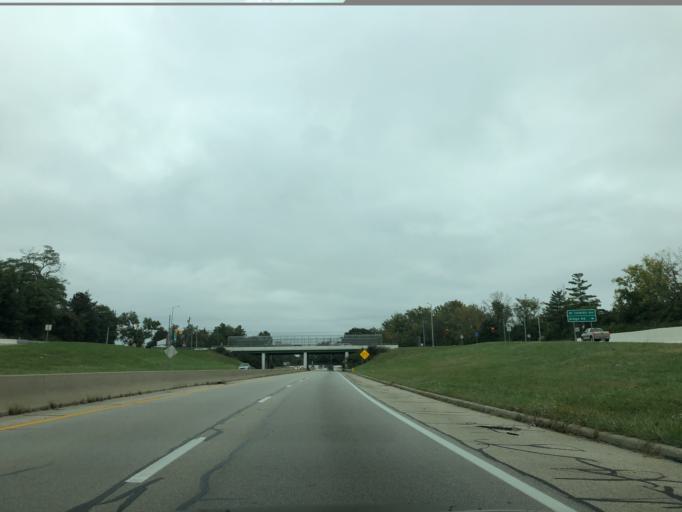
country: US
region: Ohio
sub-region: Hamilton County
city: Amberley
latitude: 39.2167
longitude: -84.4288
